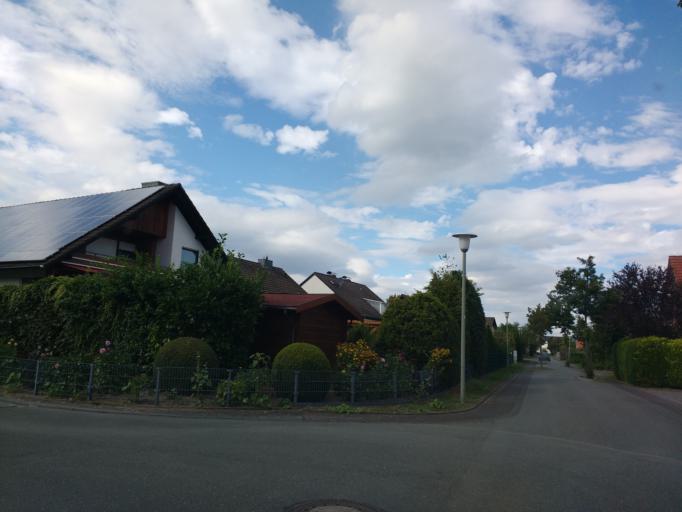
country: DE
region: North Rhine-Westphalia
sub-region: Regierungsbezirk Detmold
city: Schlangen
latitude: 51.7956
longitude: 8.8398
